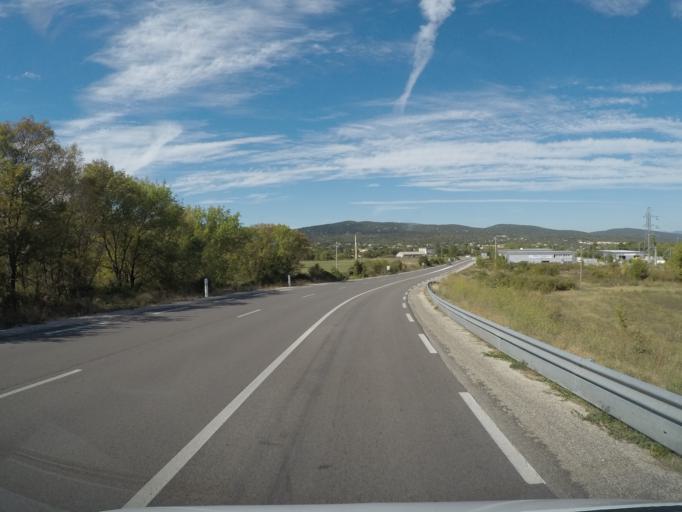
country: FR
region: Languedoc-Roussillon
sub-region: Departement de l'Herault
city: Saint-Martin-de-Londres
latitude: 43.7792
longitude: 3.7384
